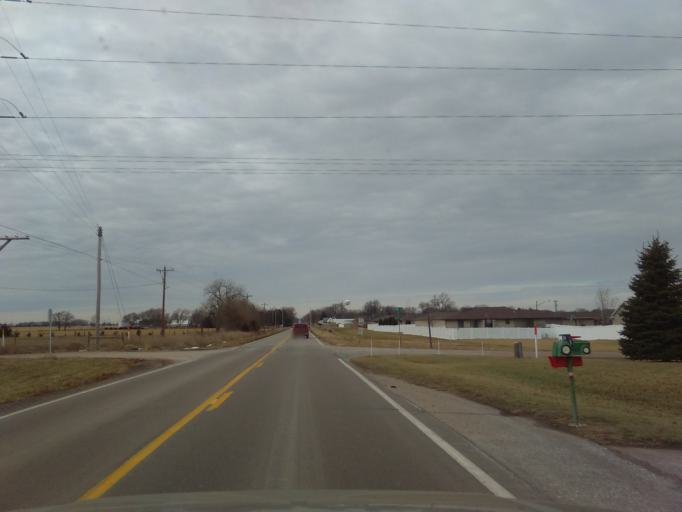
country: US
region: Nebraska
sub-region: Hall County
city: Grand Island
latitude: 40.7710
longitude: -98.3588
